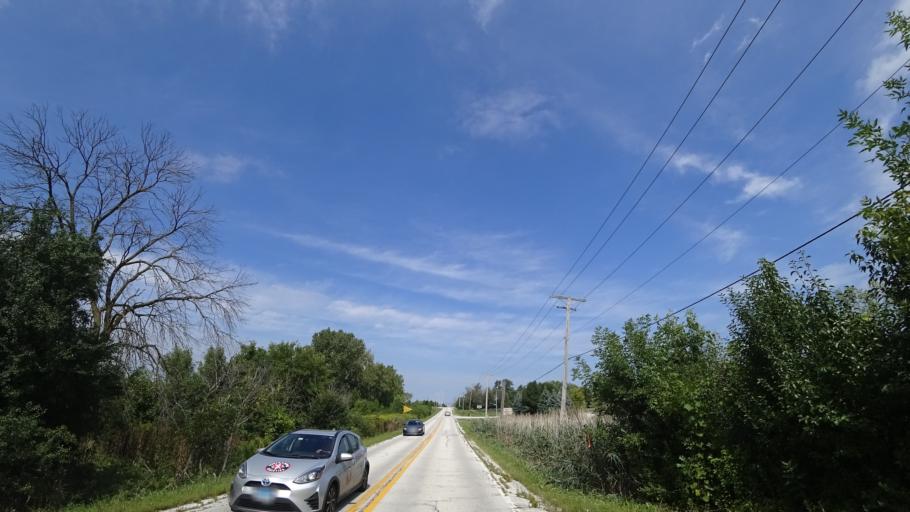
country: US
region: Illinois
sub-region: Cook County
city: Orland Hills
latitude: 41.5604
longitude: -87.8465
